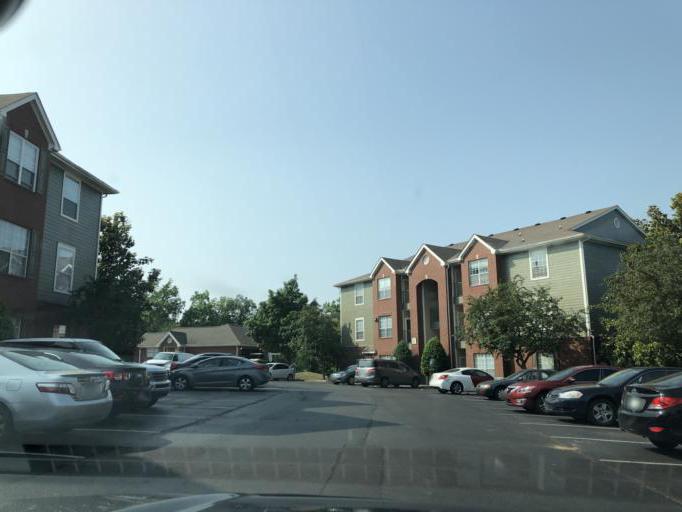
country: US
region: Tennessee
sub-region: Rutherford County
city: La Vergne
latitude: 36.0573
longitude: -86.6402
